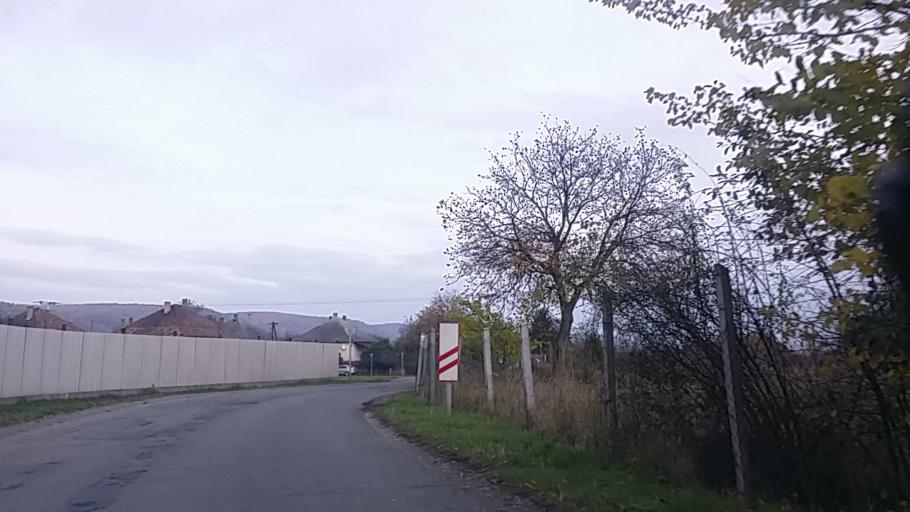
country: HU
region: Borsod-Abauj-Zemplen
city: Putnok
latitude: 48.2863
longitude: 20.4407
